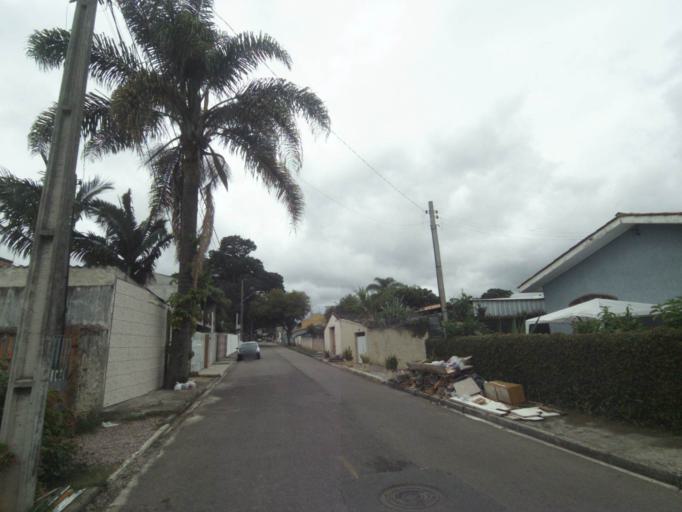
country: BR
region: Parana
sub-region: Curitiba
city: Curitiba
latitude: -25.4857
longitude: -49.3018
